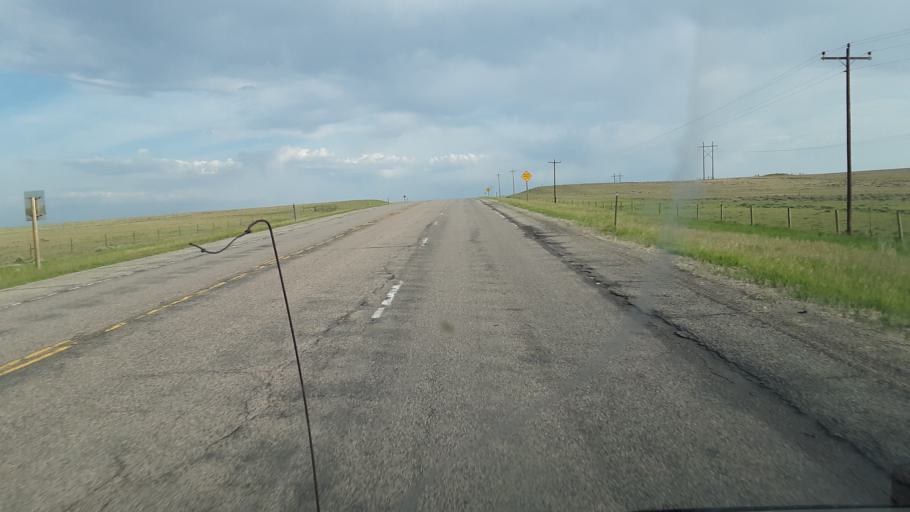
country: US
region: Wyoming
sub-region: Natrona County
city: Bar Nunn
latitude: 43.0136
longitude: -106.7378
